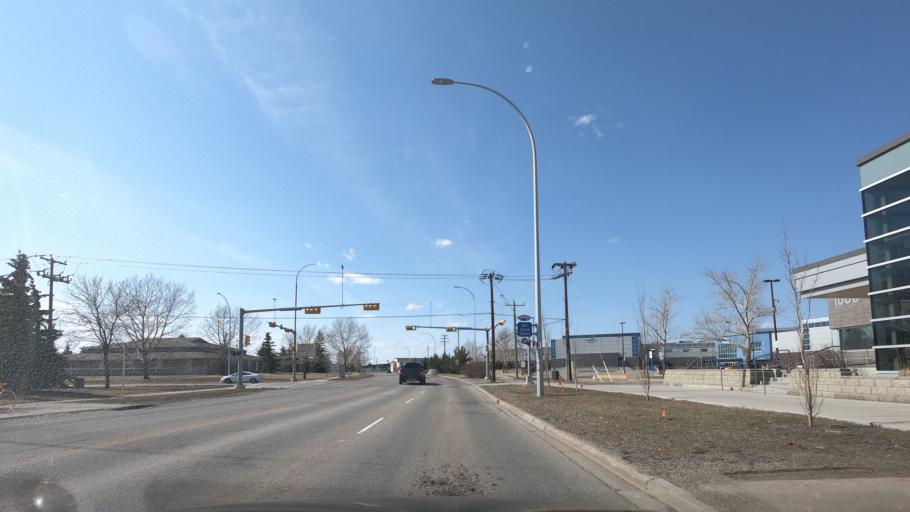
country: CA
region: Alberta
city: Airdrie
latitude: 51.2832
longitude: -113.9926
